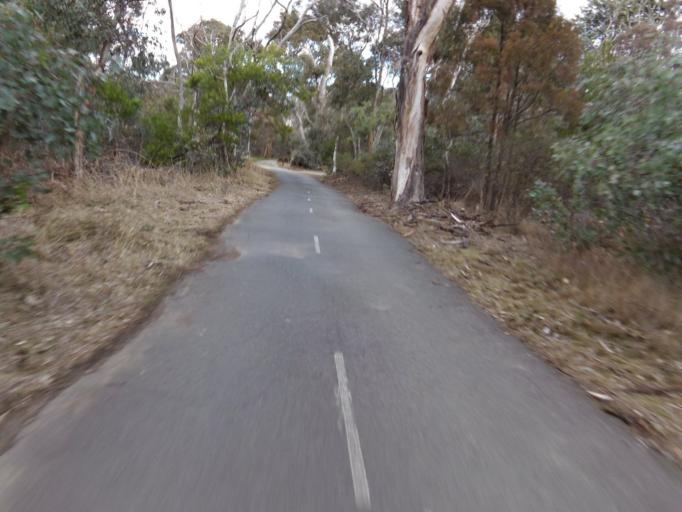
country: AU
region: Australian Capital Territory
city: Acton
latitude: -35.2551
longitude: 149.1094
